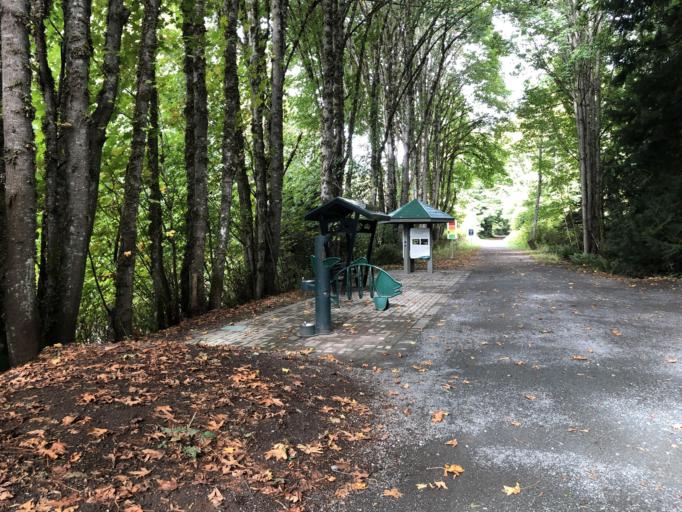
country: CA
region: British Columbia
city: Sooke
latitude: 48.4066
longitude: -123.7042
